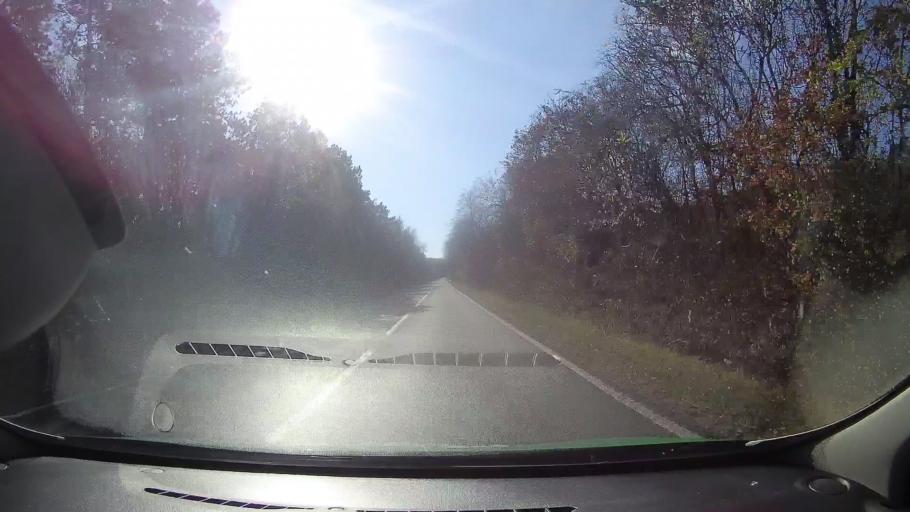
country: RO
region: Tulcea
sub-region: Oras Babadag
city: Babadag
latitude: 44.8361
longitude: 28.6953
